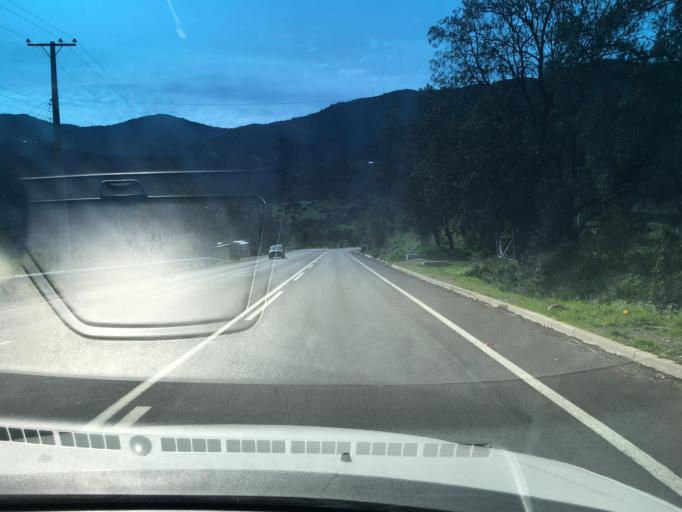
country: CL
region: Valparaiso
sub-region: Provincia de San Felipe
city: Llaillay
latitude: -33.0621
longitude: -71.0296
